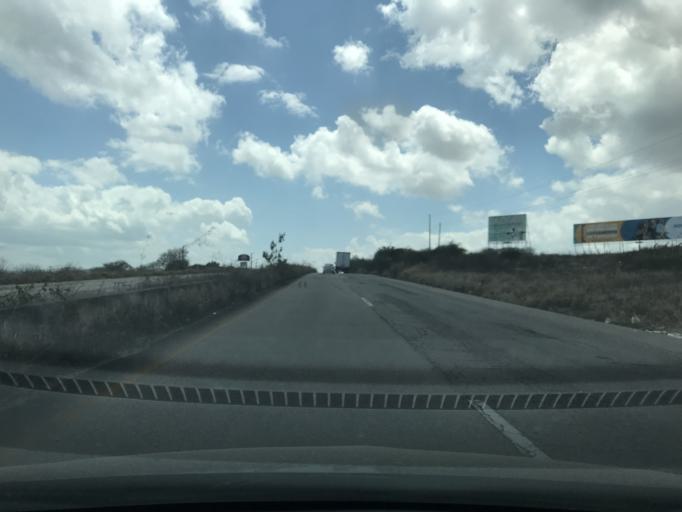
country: BR
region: Pernambuco
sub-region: Caruaru
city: Caruaru
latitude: -8.3044
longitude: -35.9289
